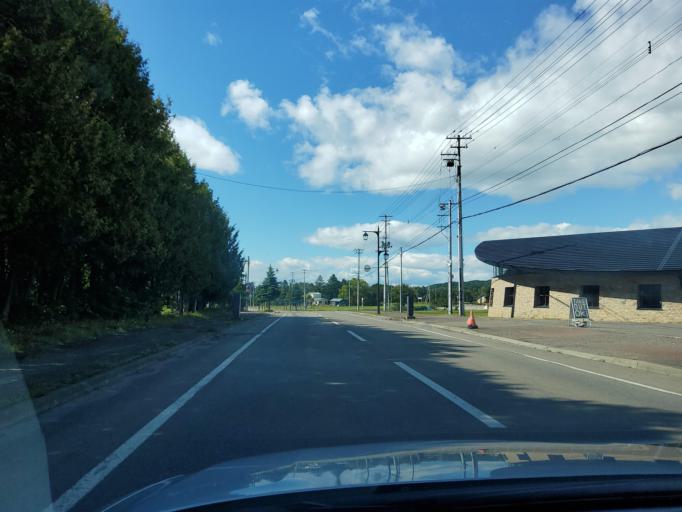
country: JP
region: Hokkaido
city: Obihiro
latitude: 42.9339
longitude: 143.2984
